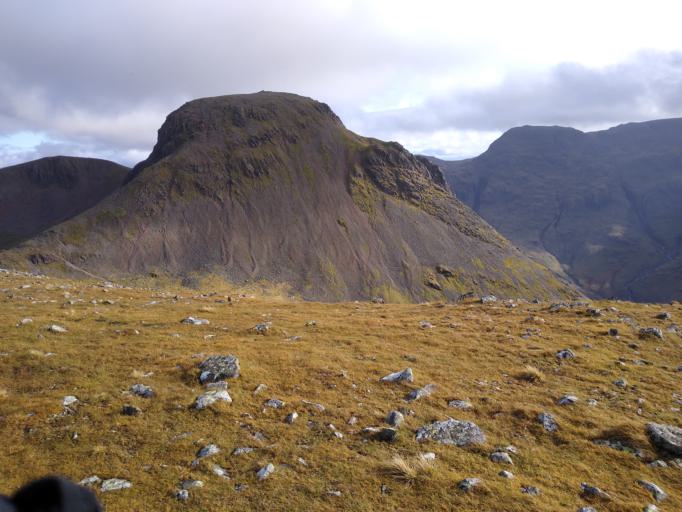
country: GB
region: England
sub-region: Cumbria
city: Keswick
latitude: 54.4842
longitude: -3.2353
